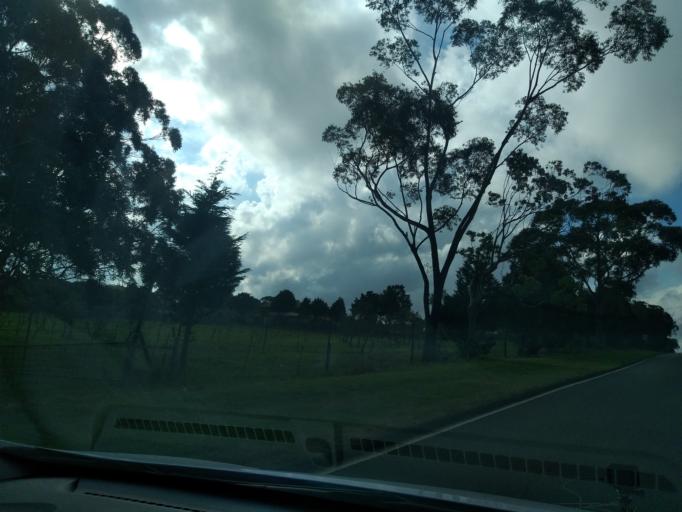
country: AU
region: New South Wales
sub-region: Wollongong
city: Helensburgh
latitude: -34.2035
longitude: 150.9794
